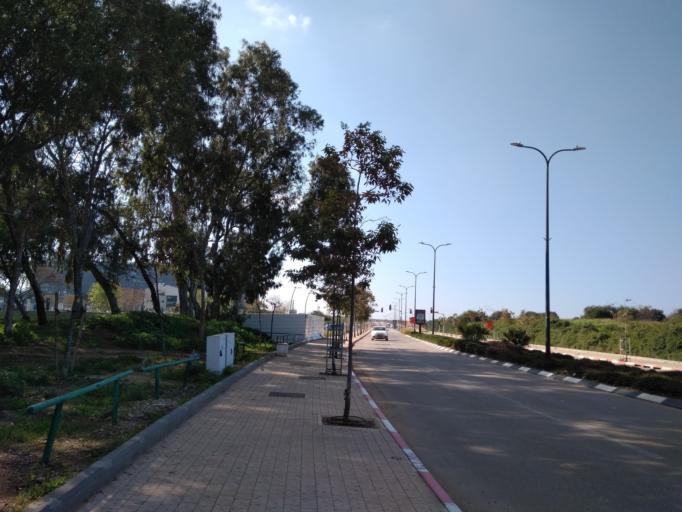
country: IL
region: Tel Aviv
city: Herzliya Pituah
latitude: 32.1608
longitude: 34.8055
